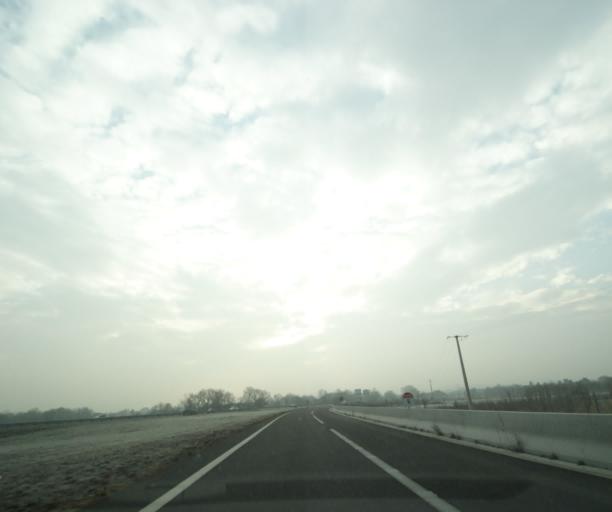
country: FR
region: Rhone-Alpes
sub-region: Departement du Rhone
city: Les Cheres
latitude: 45.8936
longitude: 4.7319
